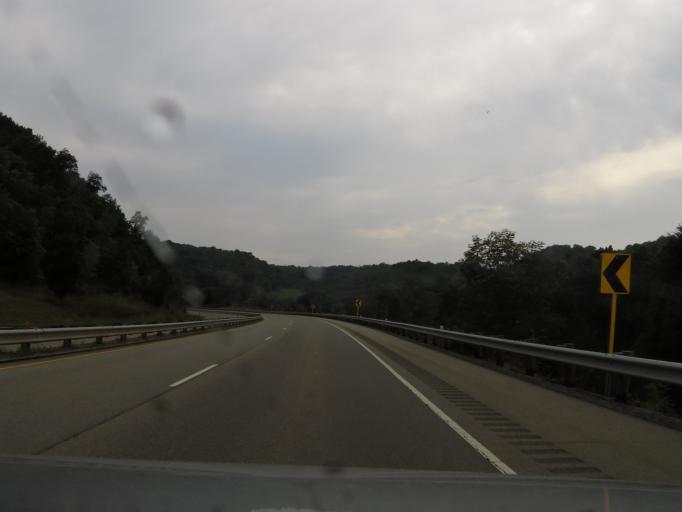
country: US
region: Ohio
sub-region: Brown County
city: Ripley
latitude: 38.7603
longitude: -83.8254
